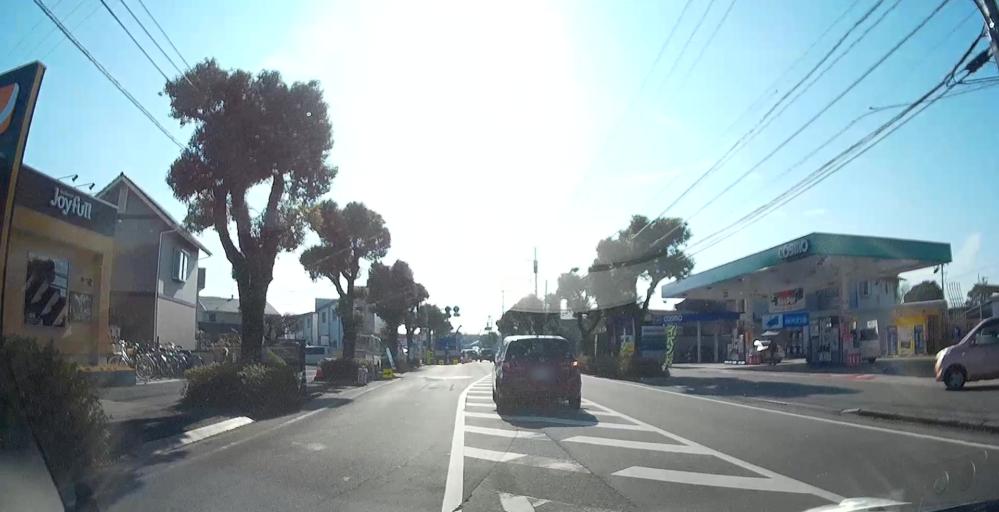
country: JP
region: Kumamoto
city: Kumamoto
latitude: 32.7480
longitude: 130.6840
